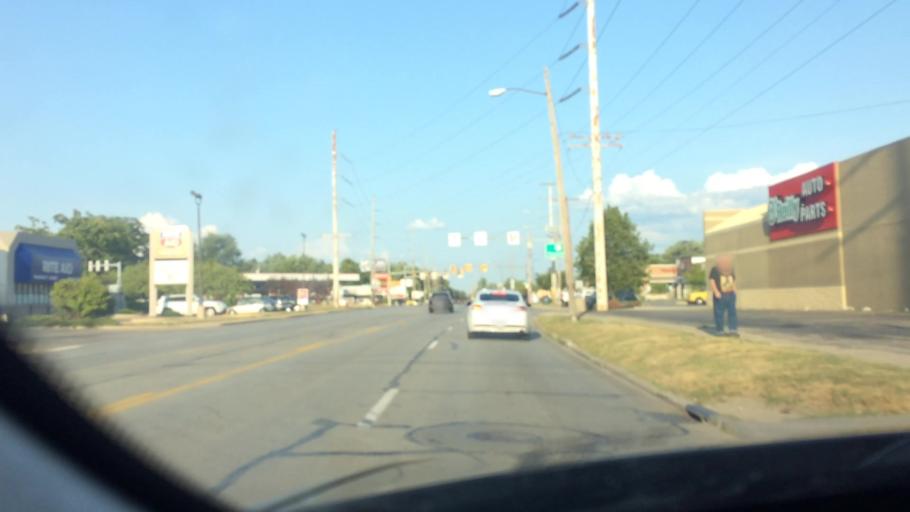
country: US
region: Ohio
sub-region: Lucas County
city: Ottawa Hills
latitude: 41.6534
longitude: -83.6667
